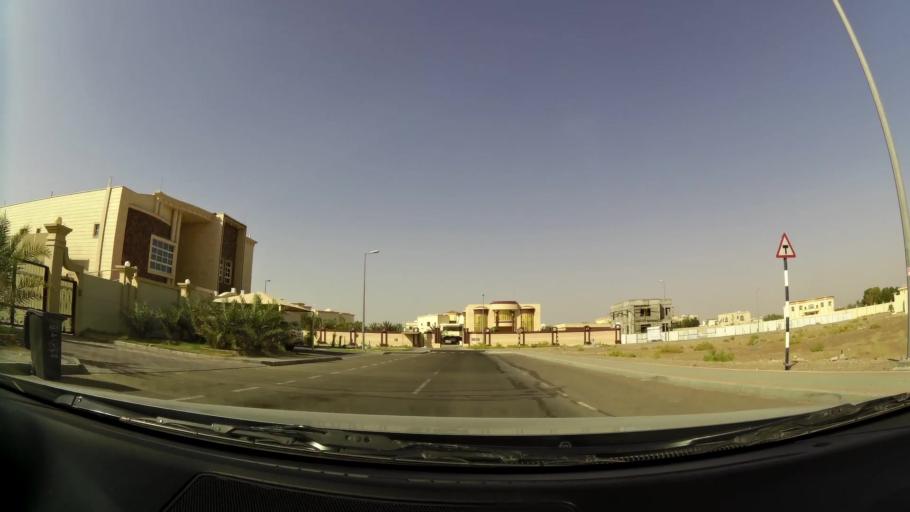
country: OM
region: Al Buraimi
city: Al Buraymi
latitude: 24.3519
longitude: 55.7925
